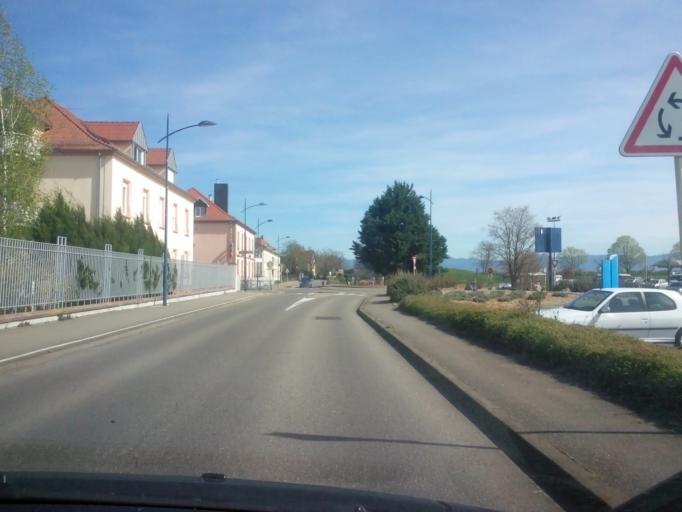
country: FR
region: Alsace
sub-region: Departement du Haut-Rhin
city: Neuf-Brisach
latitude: 48.0112
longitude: 7.5413
